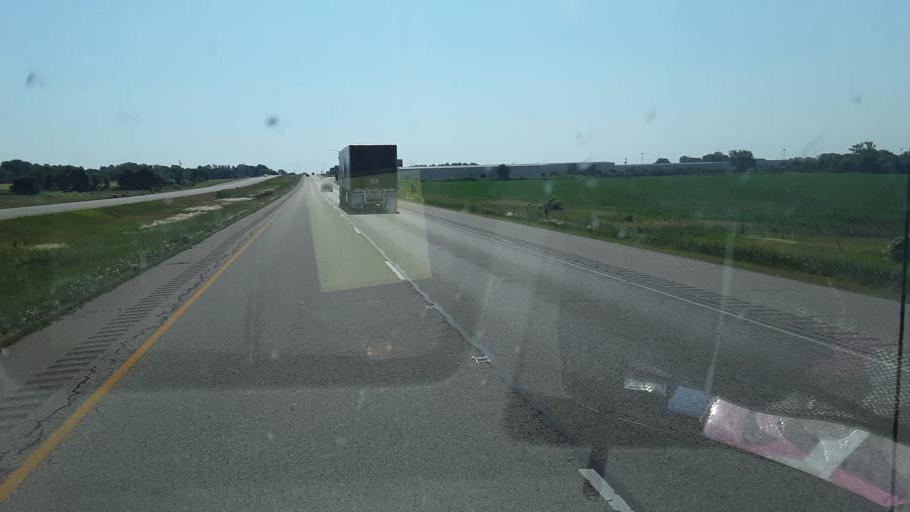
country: US
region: Illinois
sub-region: McLean County
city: Bloomington
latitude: 40.4360
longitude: -88.9989
